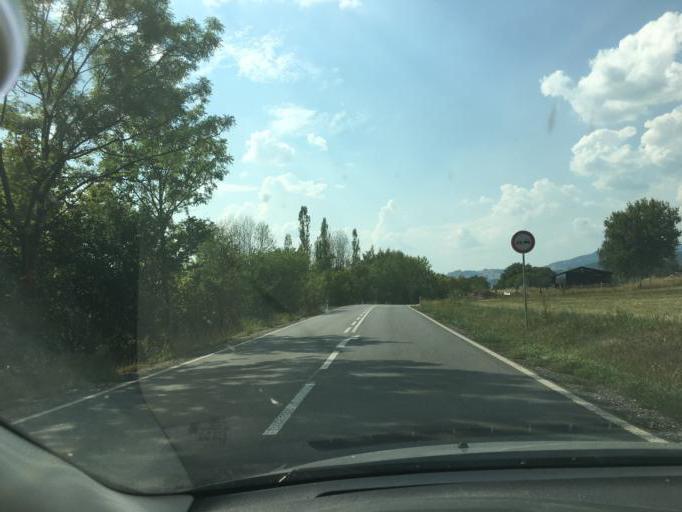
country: CZ
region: Kralovehradecky
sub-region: Okres Trutnov
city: Rudnik
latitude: 50.6153
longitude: 15.6782
